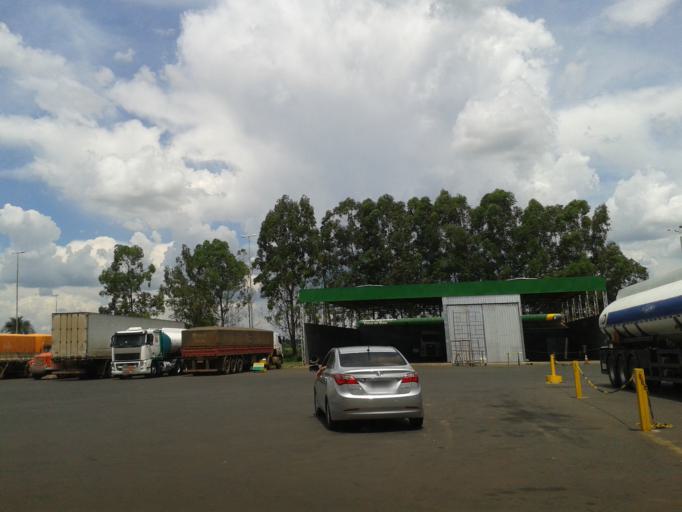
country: BR
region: Minas Gerais
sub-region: Uberlandia
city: Uberlandia
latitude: -18.8934
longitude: -48.4187
